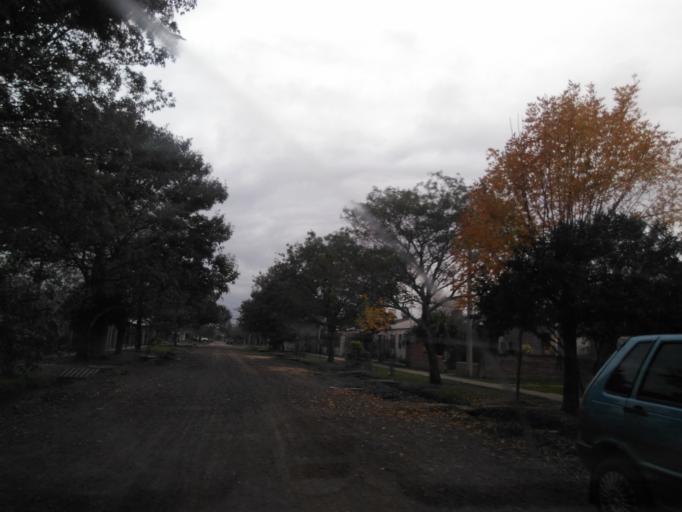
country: AR
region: Chaco
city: Fontana
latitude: -27.3974
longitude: -58.9938
